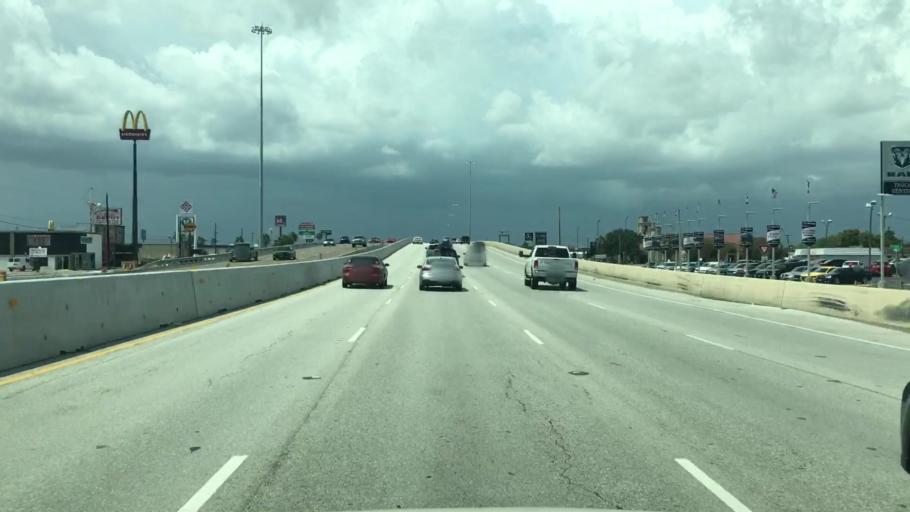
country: US
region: Texas
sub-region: Nueces County
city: Corpus Christi
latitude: 27.7273
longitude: -97.4101
